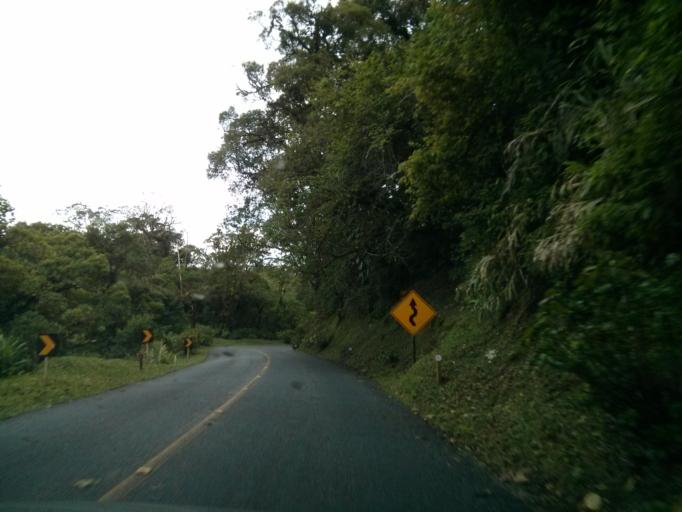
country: BR
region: Parana
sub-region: Campina Grande Do Sul
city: Campina Grande do Sul
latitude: -25.3350
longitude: -48.8973
